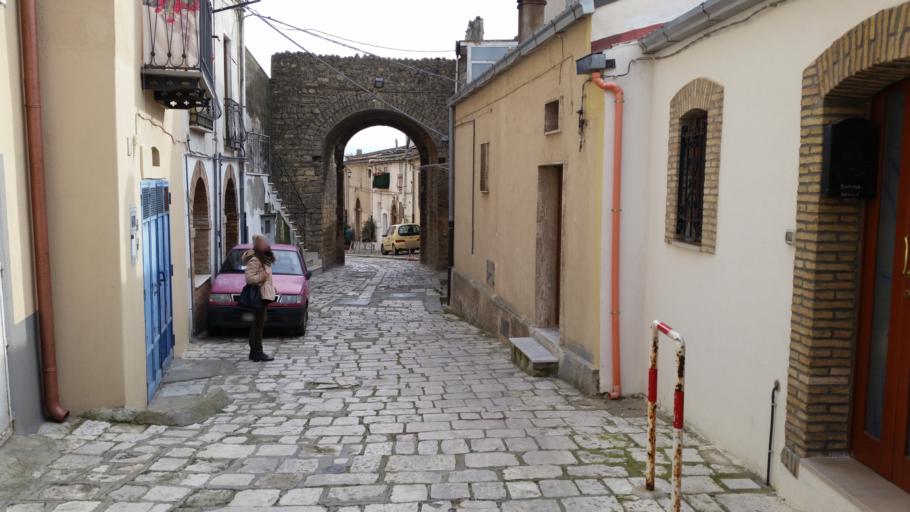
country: IT
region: Basilicate
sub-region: Provincia di Matera
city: Tricarico
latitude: 40.6206
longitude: 16.1464
